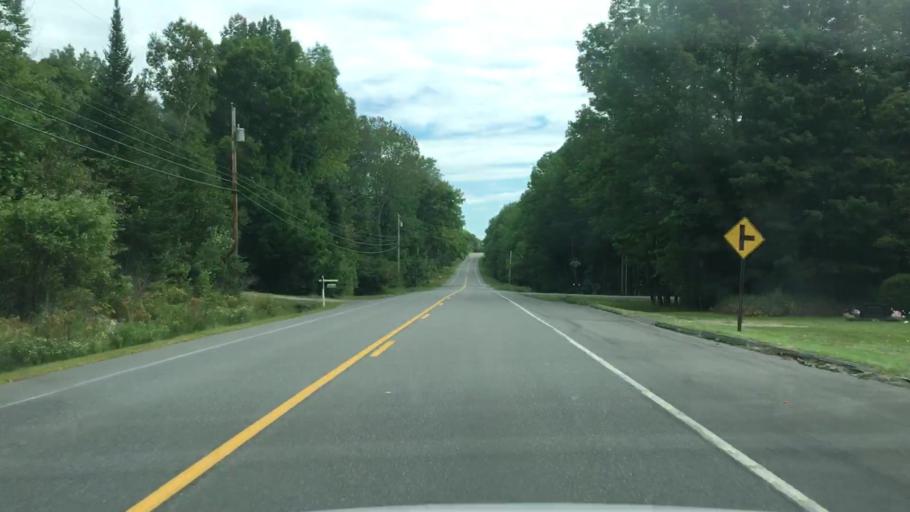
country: US
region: Maine
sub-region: Piscataquis County
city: Brownville
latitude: 45.2268
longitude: -69.1156
